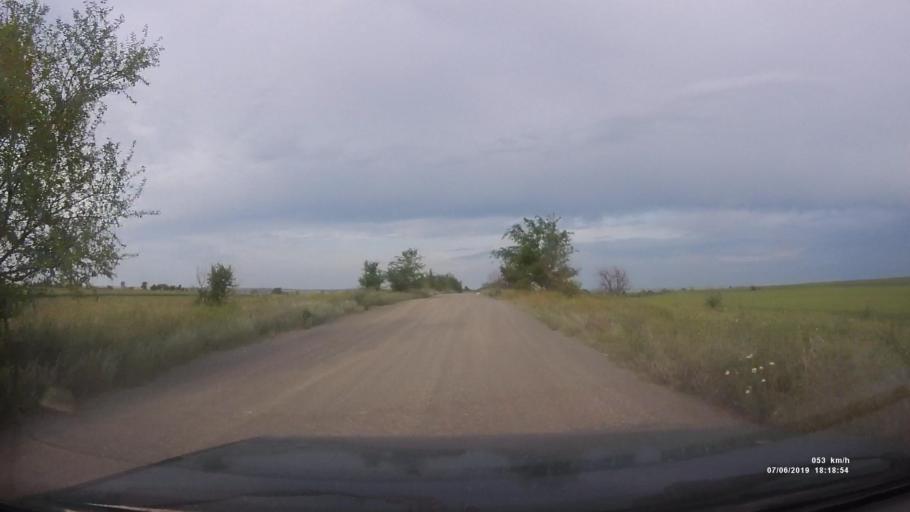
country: RU
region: Rostov
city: Staraya Stanitsa
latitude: 48.2559
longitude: 40.3663
